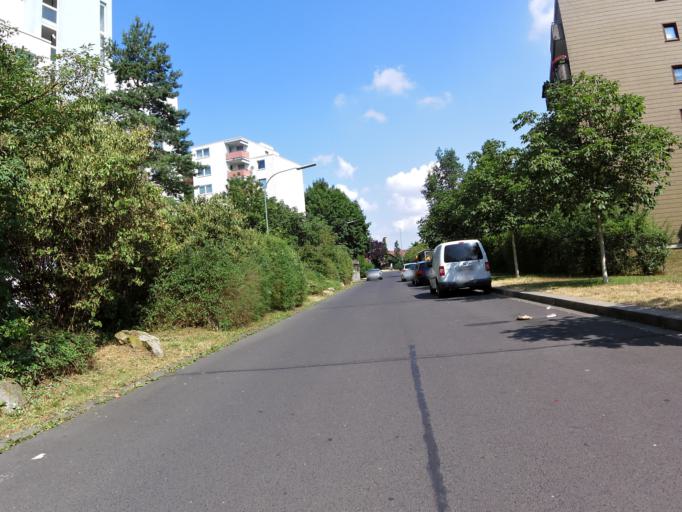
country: DE
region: Bavaria
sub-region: Regierungsbezirk Unterfranken
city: Randersacker
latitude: 49.7496
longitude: 9.9575
